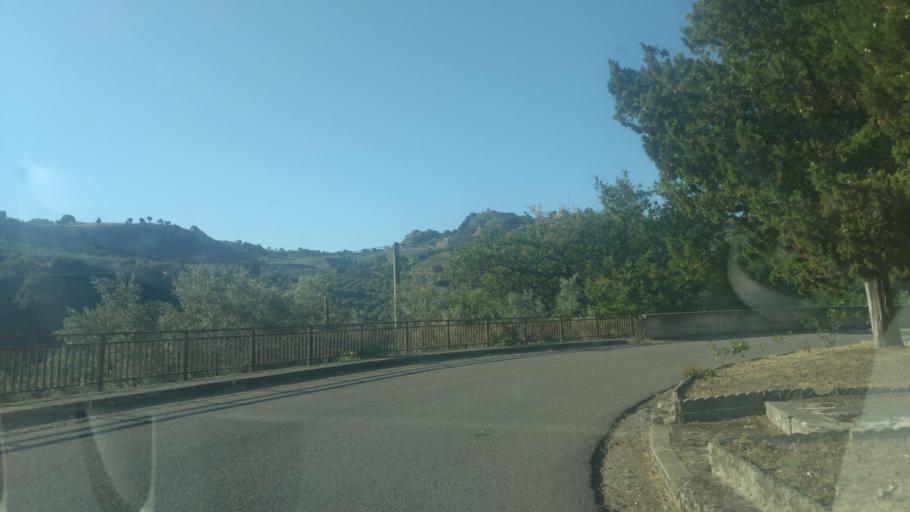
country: IT
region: Calabria
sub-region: Provincia di Catanzaro
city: Squillace
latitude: 38.7761
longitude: 16.5100
